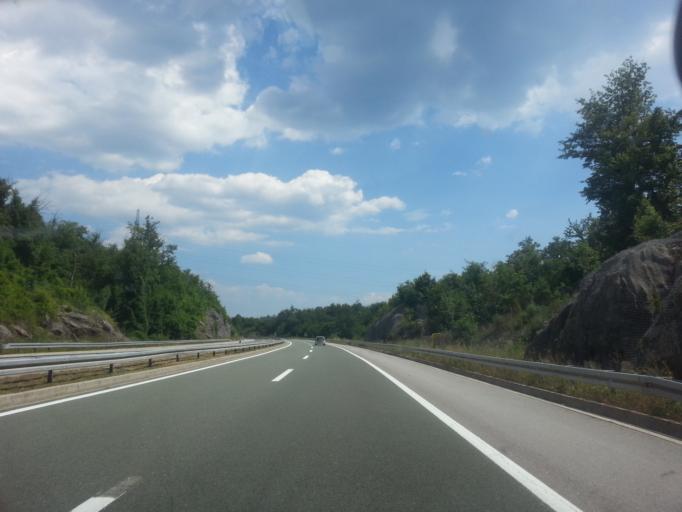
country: HR
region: Primorsko-Goranska
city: Matulji
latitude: 45.3839
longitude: 14.3032
